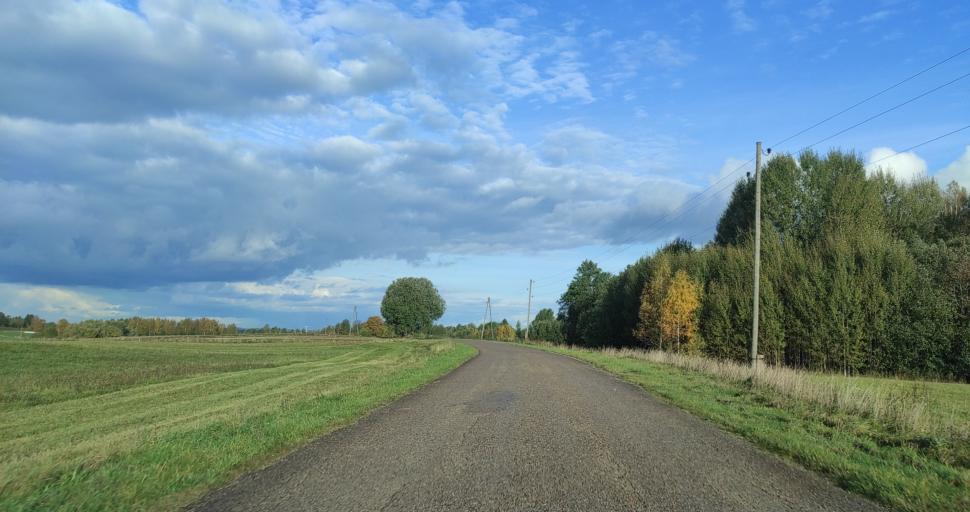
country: LV
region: Aizpute
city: Aizpute
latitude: 56.7752
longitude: 21.7824
